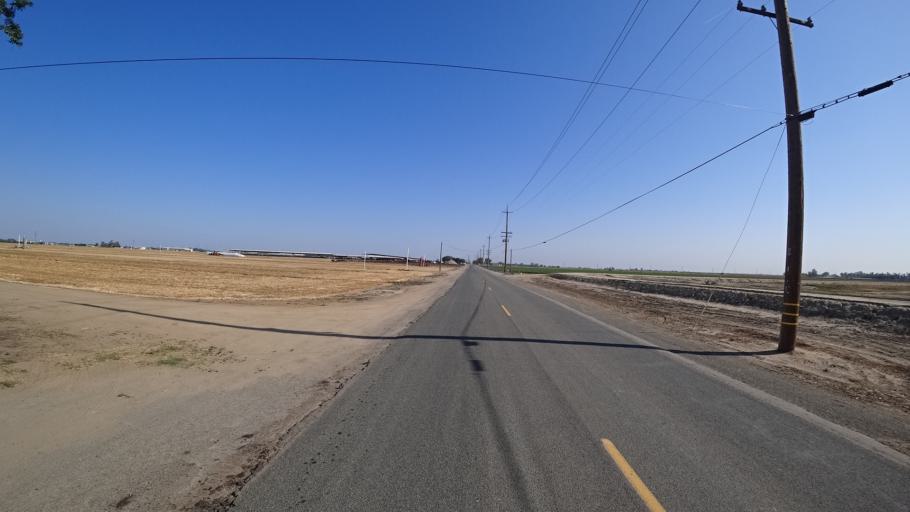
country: US
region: California
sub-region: Kings County
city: Home Garden
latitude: 36.2903
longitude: -119.5832
